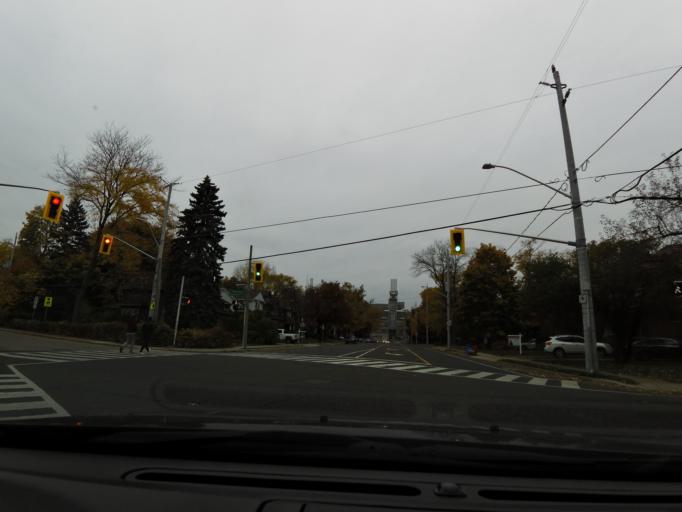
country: CA
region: Ontario
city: Hamilton
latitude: 43.2603
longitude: -79.9129
